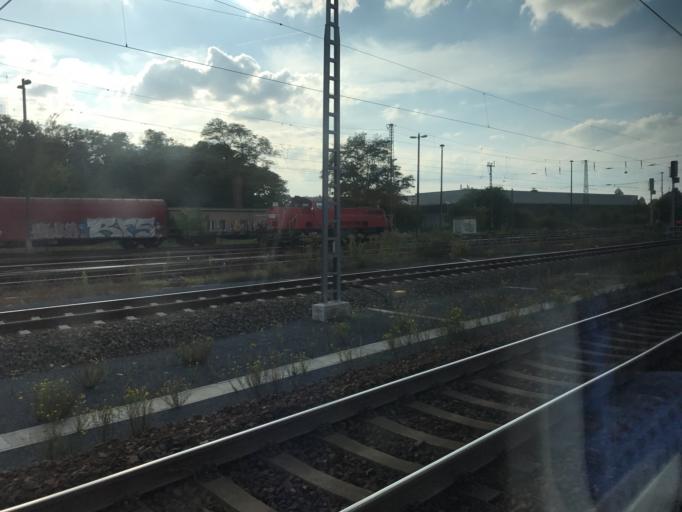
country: DE
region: Saxony
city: Coswig
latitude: 51.1215
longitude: 13.5826
